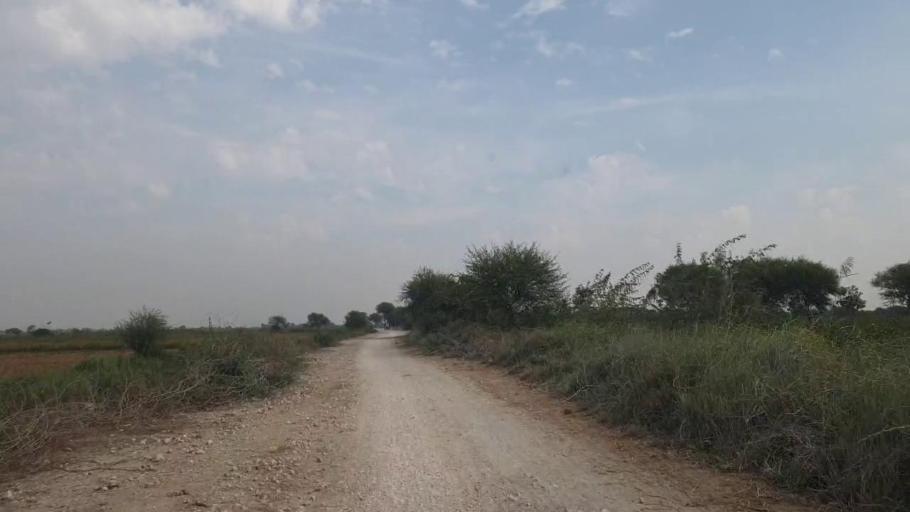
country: PK
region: Sindh
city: Rajo Khanani
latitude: 24.9580
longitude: 68.9950
